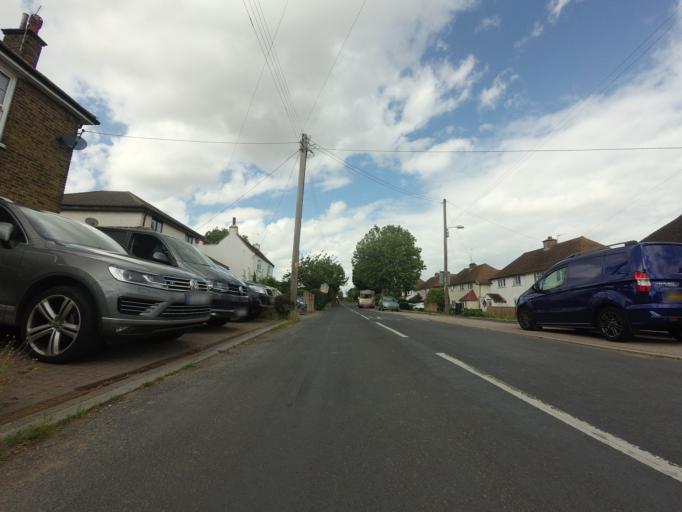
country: GB
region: England
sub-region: Medway
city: Allhallows
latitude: 51.4559
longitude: 0.6362
